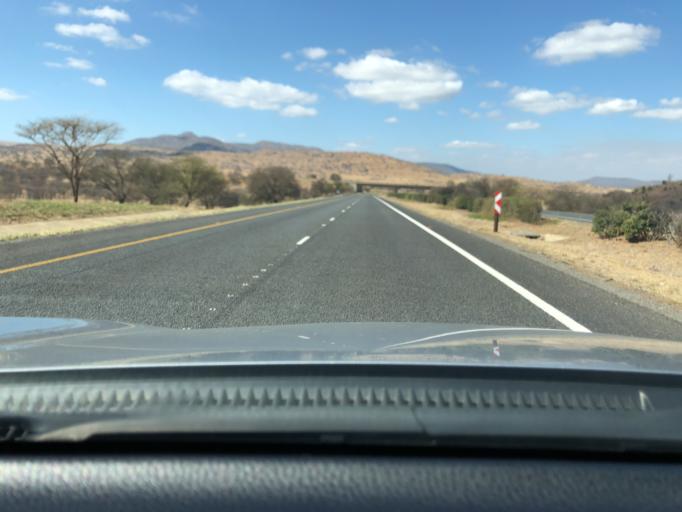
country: ZA
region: KwaZulu-Natal
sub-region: uThukela District Municipality
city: Ladysmith
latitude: -28.6636
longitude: 29.6323
